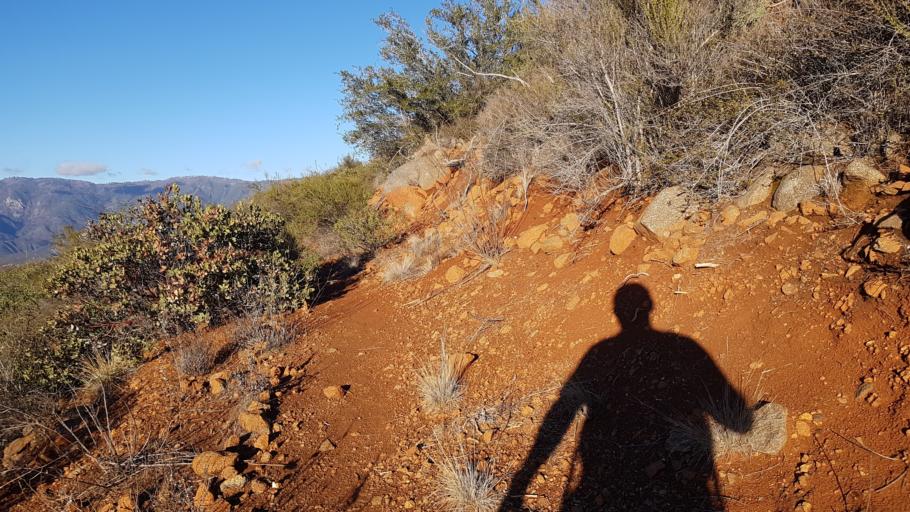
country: US
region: California
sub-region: San Diego County
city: Valley Center
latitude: 33.2395
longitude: -116.9343
